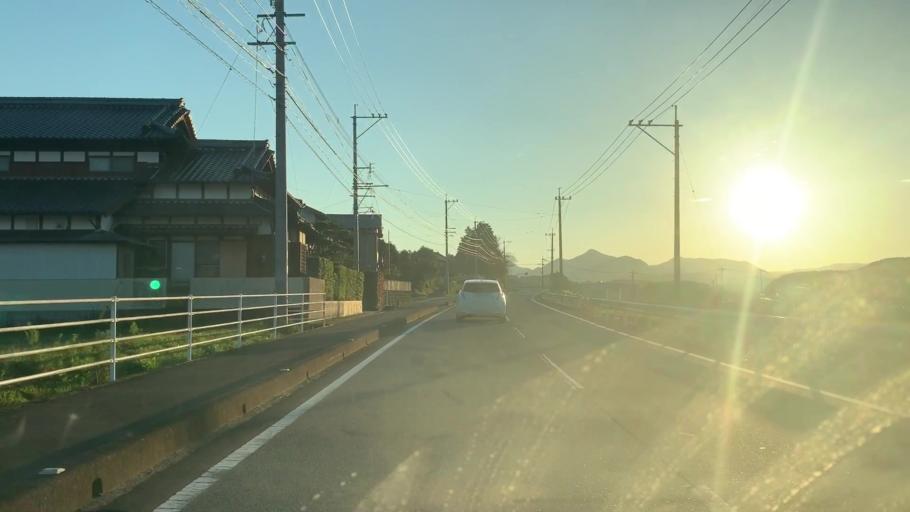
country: JP
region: Saga Prefecture
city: Imaricho-ko
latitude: 33.2822
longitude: 129.9687
